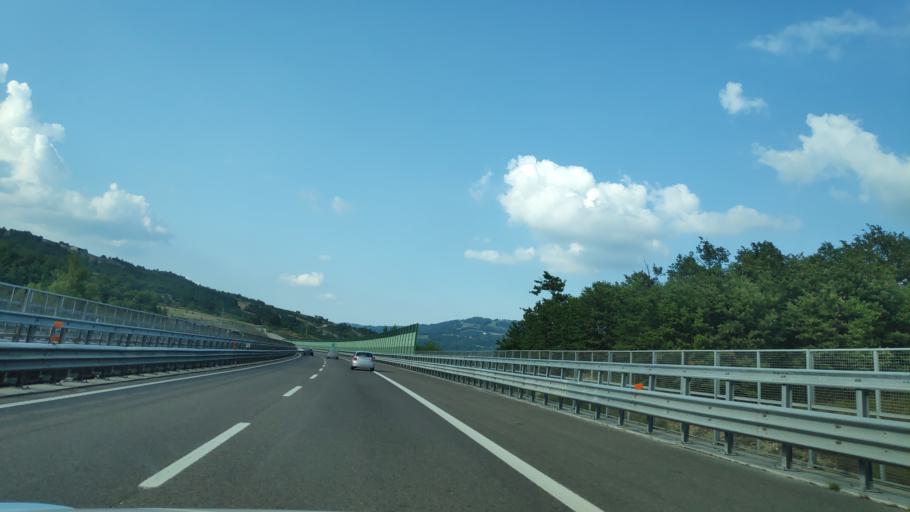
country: IT
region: Emilia-Romagna
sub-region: Provincia di Bologna
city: Castiglione dei Pepoli
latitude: 44.1614
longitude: 11.1972
